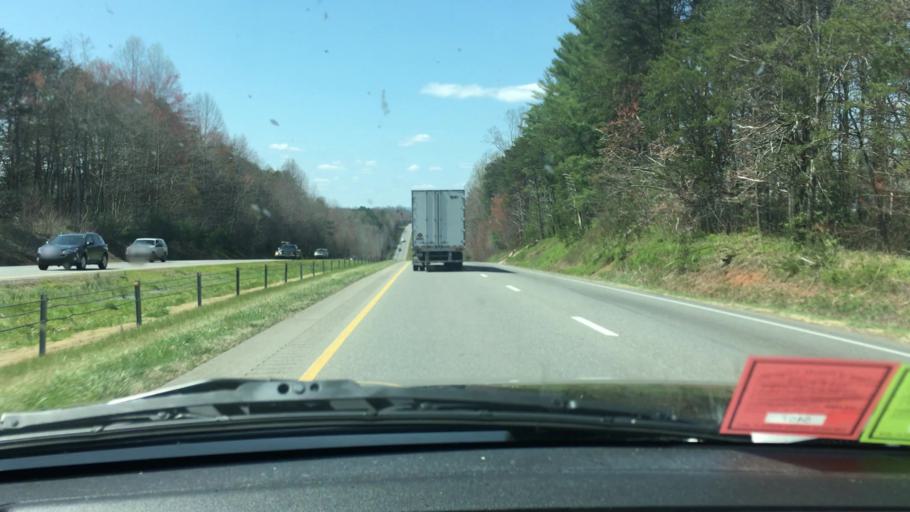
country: US
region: North Carolina
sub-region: Surry County
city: Pilot Mountain
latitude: 36.4217
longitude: -80.5154
